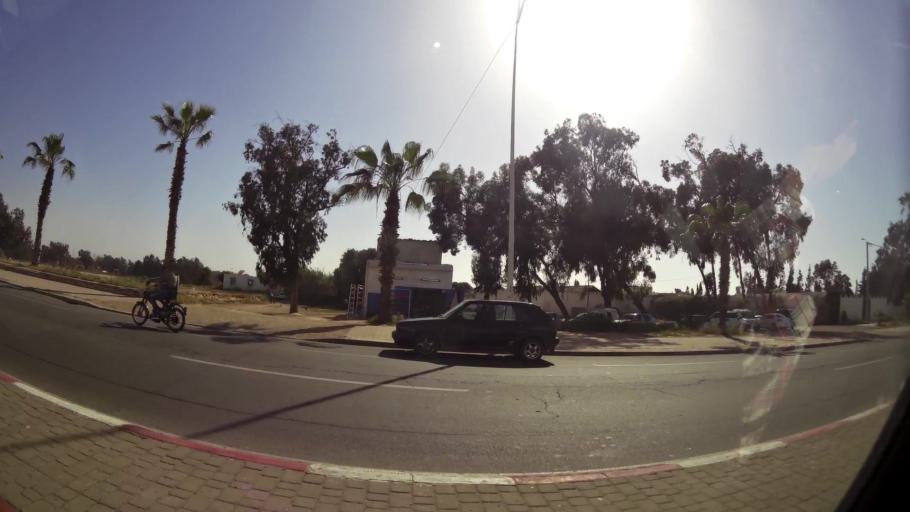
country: MA
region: Oued ed Dahab-Lagouira
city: Dakhla
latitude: 30.3849
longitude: -9.5716
